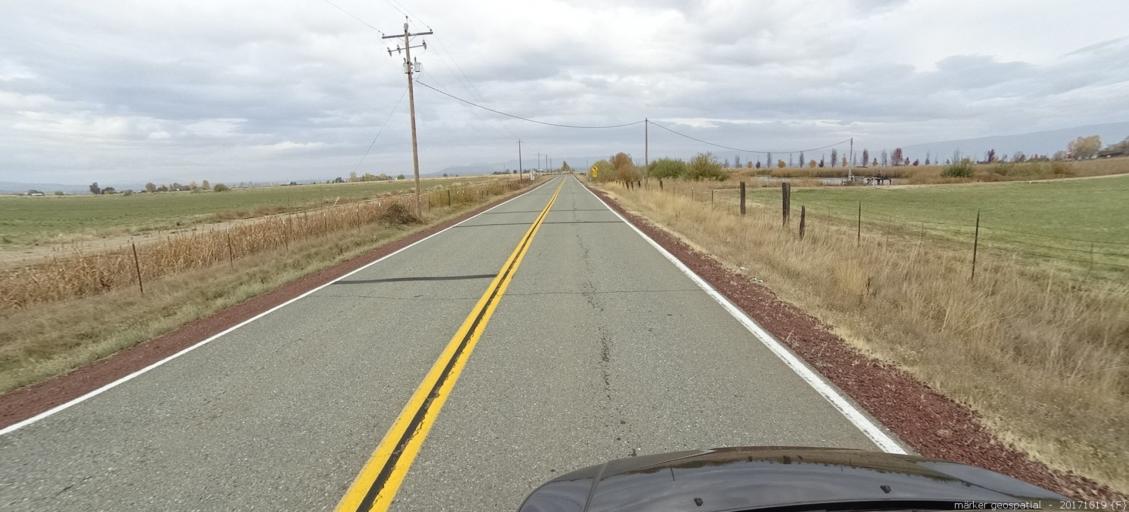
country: US
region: California
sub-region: Shasta County
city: Burney
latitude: 41.0547
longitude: -121.4612
